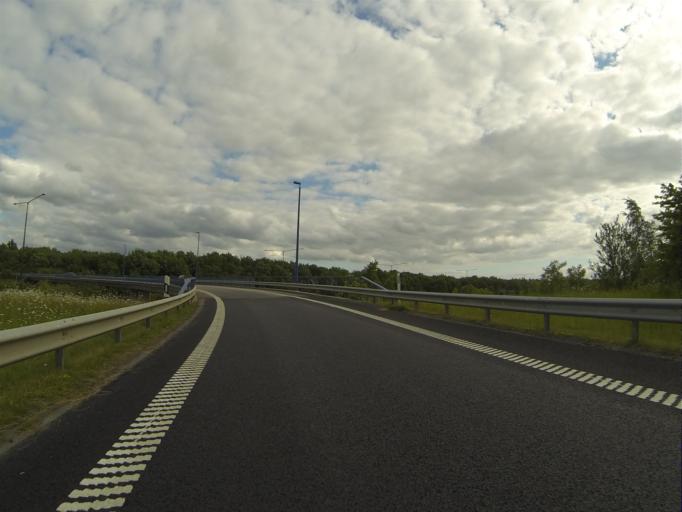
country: SE
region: Skane
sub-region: Burlovs Kommun
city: Arloev
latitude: 55.6038
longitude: 13.0678
